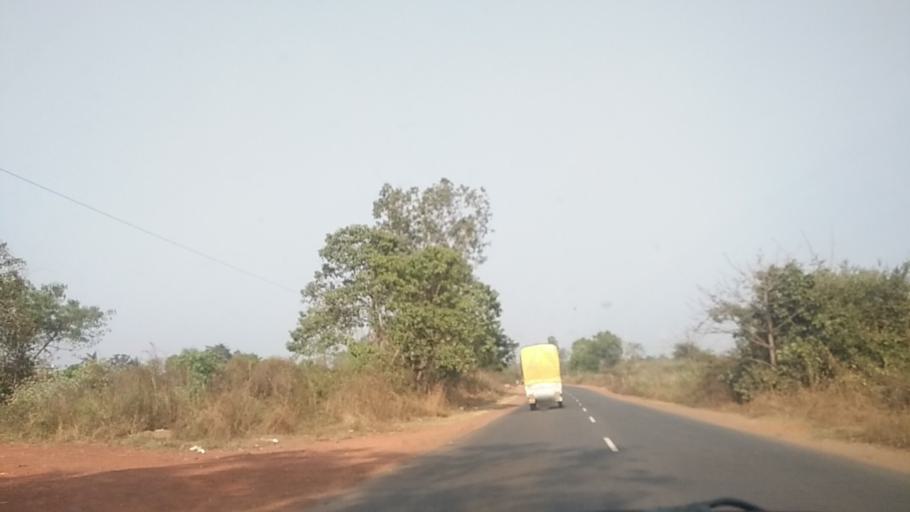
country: IN
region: Goa
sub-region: North Goa
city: Colovale
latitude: 15.6258
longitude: 73.8242
